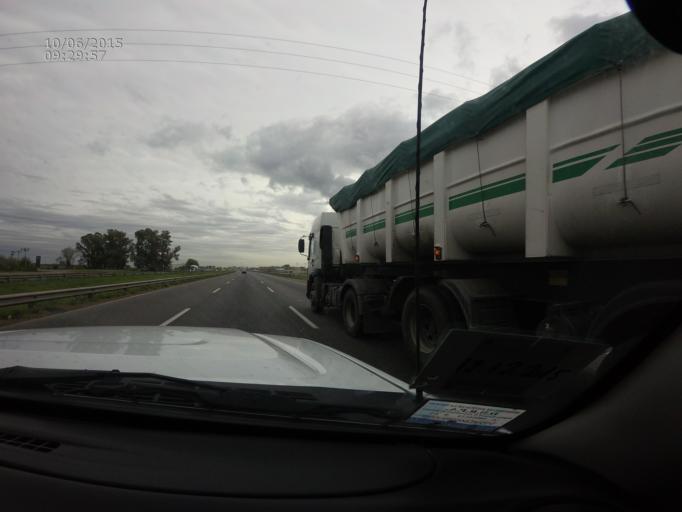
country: AR
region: Buenos Aires
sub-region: Partido de Zarate
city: Zarate
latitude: -34.1450
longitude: -59.0366
